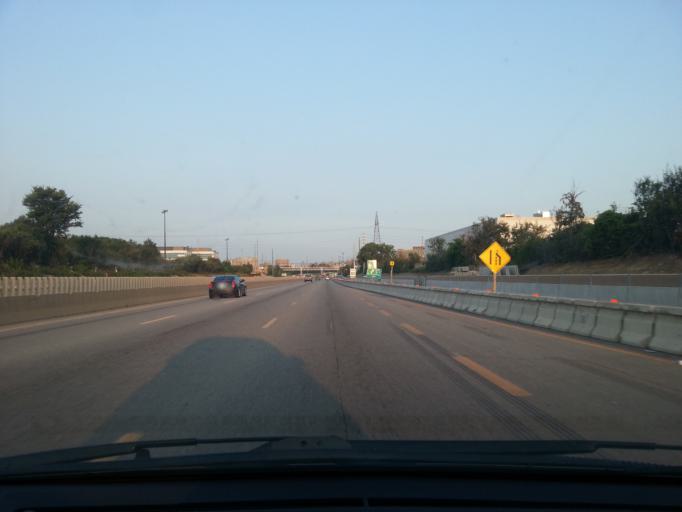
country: CA
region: Ontario
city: Ottawa
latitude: 45.4198
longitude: -75.6431
